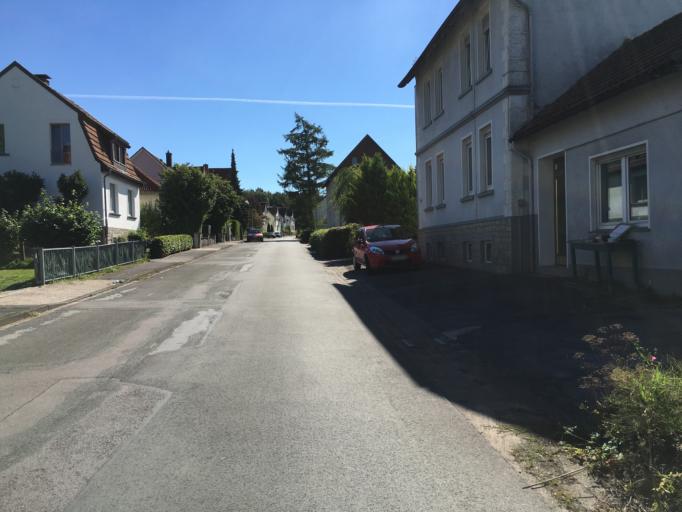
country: DE
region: North Rhine-Westphalia
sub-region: Regierungsbezirk Detmold
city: Detmold
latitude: 51.9291
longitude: 8.8444
